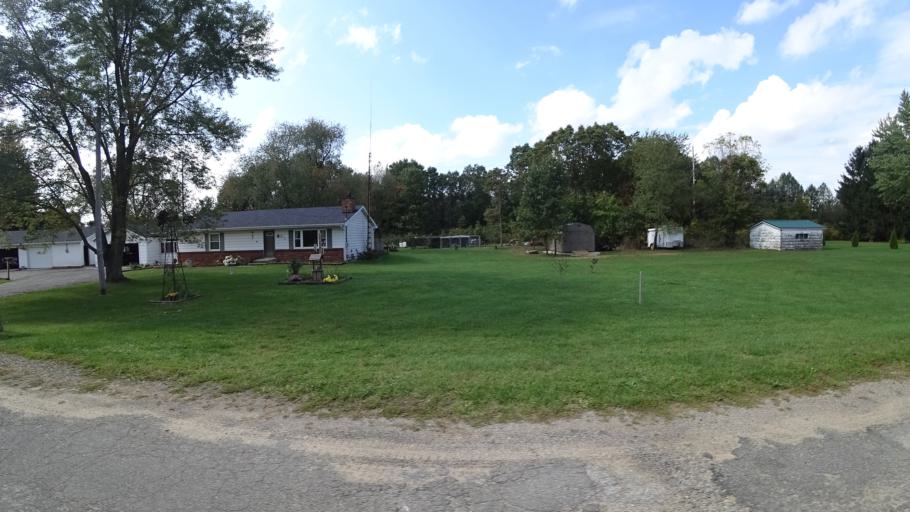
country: US
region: Michigan
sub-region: Saint Joseph County
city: Three Rivers
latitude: 41.9373
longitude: -85.6054
